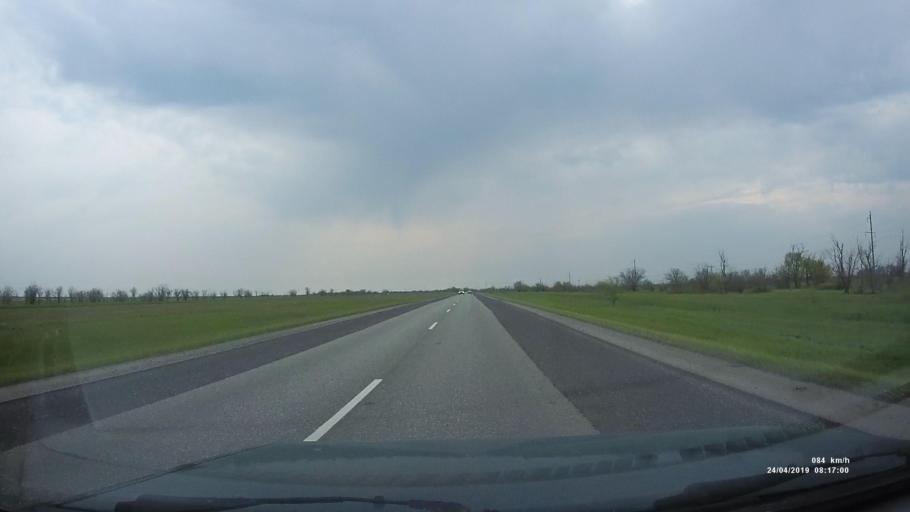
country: RU
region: Kalmykiya
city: Priyutnoye
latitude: 46.0983
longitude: 43.6222
